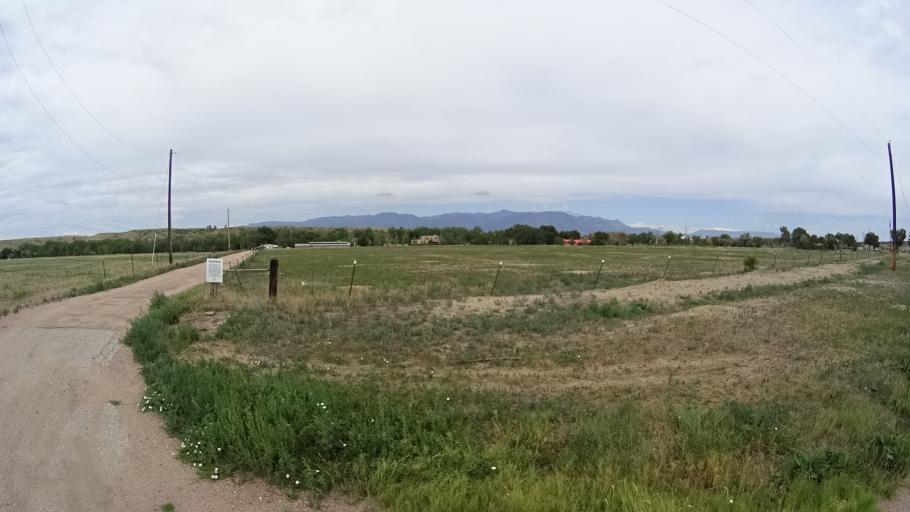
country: US
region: Colorado
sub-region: El Paso County
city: Fountain
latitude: 38.6620
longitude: -104.6915
